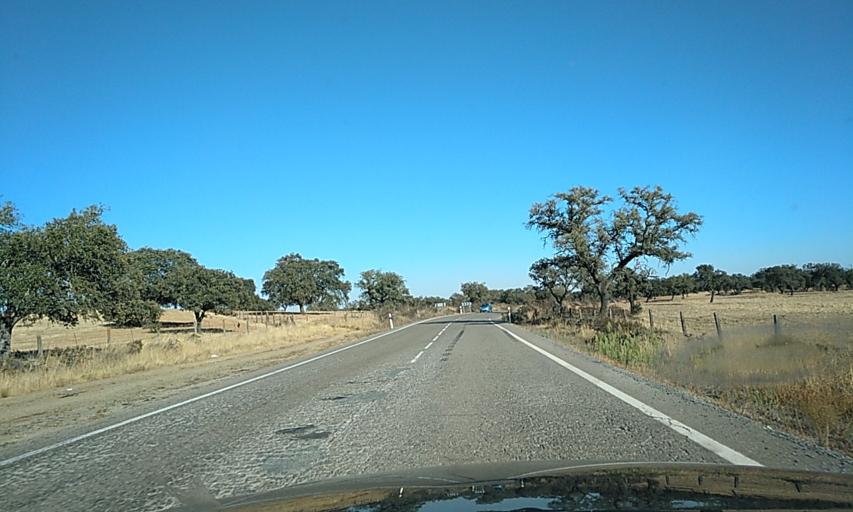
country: ES
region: Andalusia
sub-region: Provincia de Huelva
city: Santa Barbara de Casa
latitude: 37.7718
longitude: -7.1447
